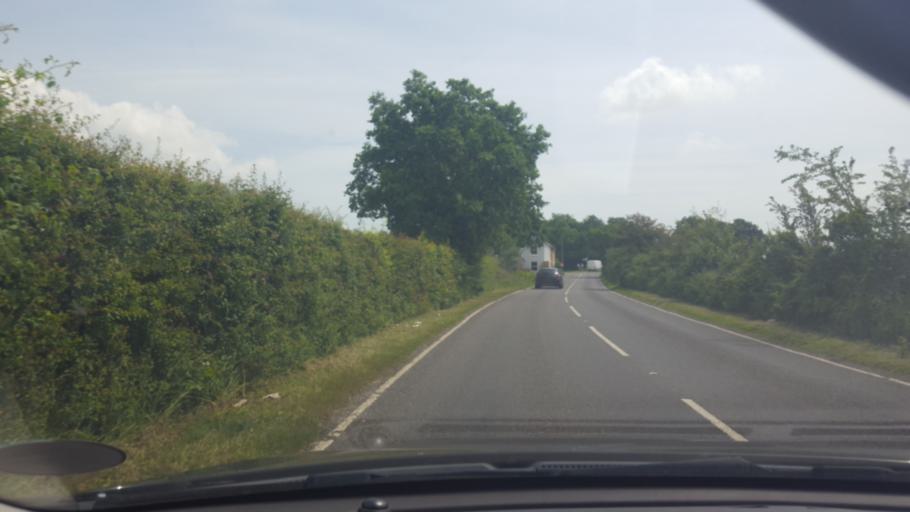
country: GB
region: England
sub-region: Essex
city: Little Clacton
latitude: 51.8733
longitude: 1.1402
